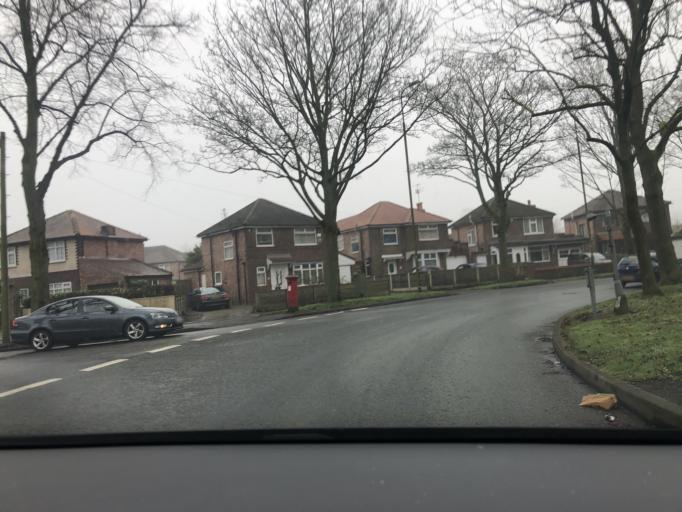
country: GB
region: England
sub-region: Trafford
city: Urmston
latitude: 53.4550
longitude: -2.3601
